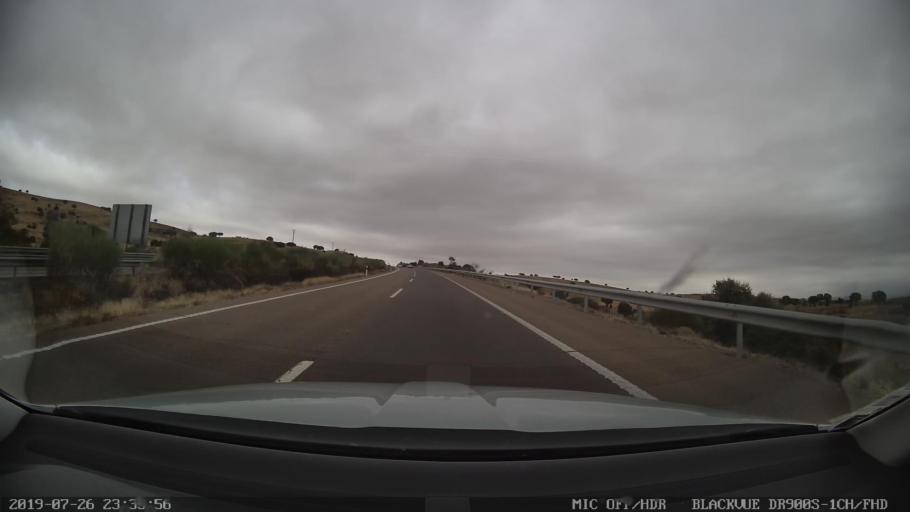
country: ES
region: Extremadura
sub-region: Provincia de Caceres
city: Santa Cruz de la Sierra
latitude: 39.3507
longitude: -5.8590
